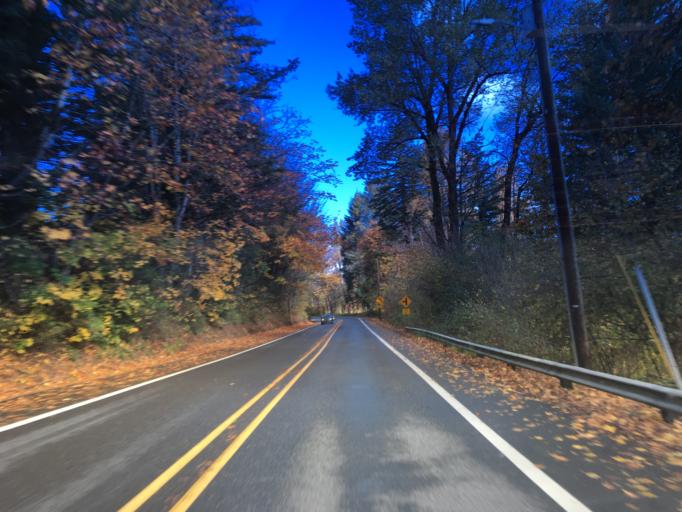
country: US
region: Oregon
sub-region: Multnomah County
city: Troutdale
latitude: 45.5139
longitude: -122.3752
